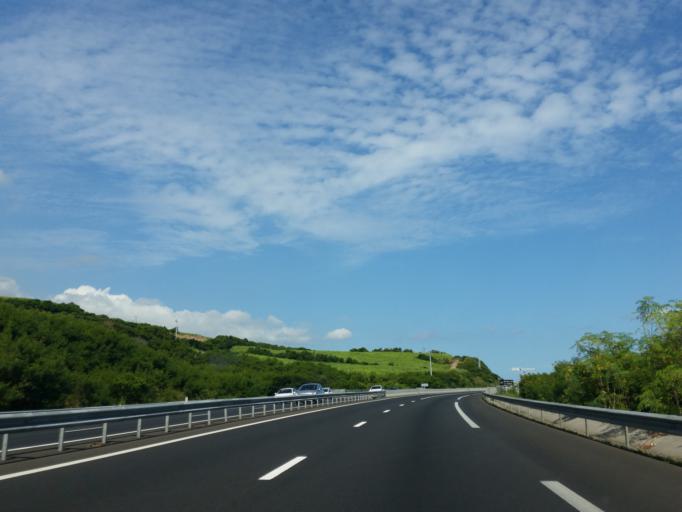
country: RE
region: Reunion
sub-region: Reunion
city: Trois-Bassins
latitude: -21.0824
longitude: 55.2557
